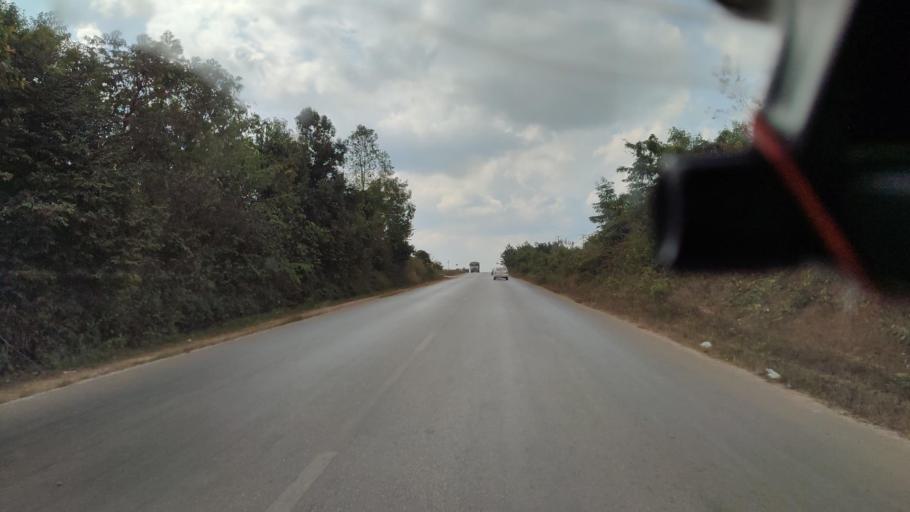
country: MM
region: Shan
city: Lashio
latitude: 22.9477
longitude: 97.6963
